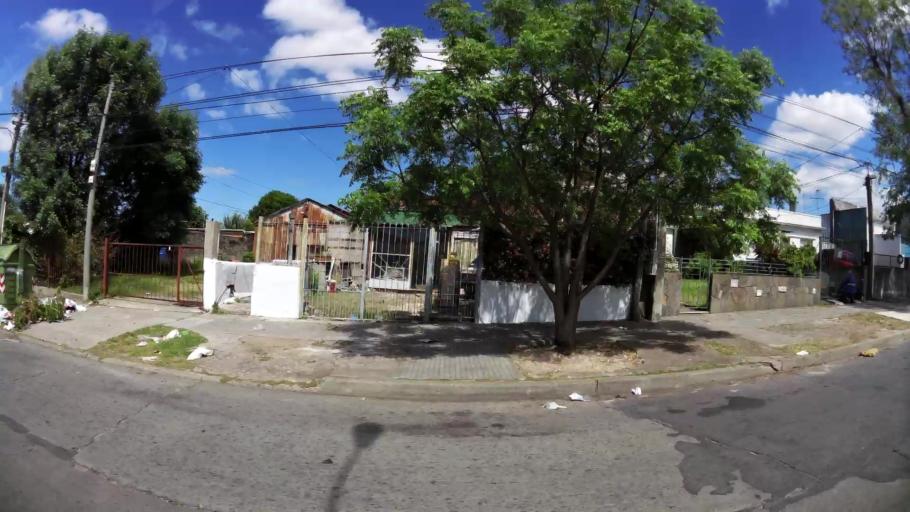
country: UY
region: Montevideo
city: Montevideo
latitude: -34.8559
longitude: -56.1442
